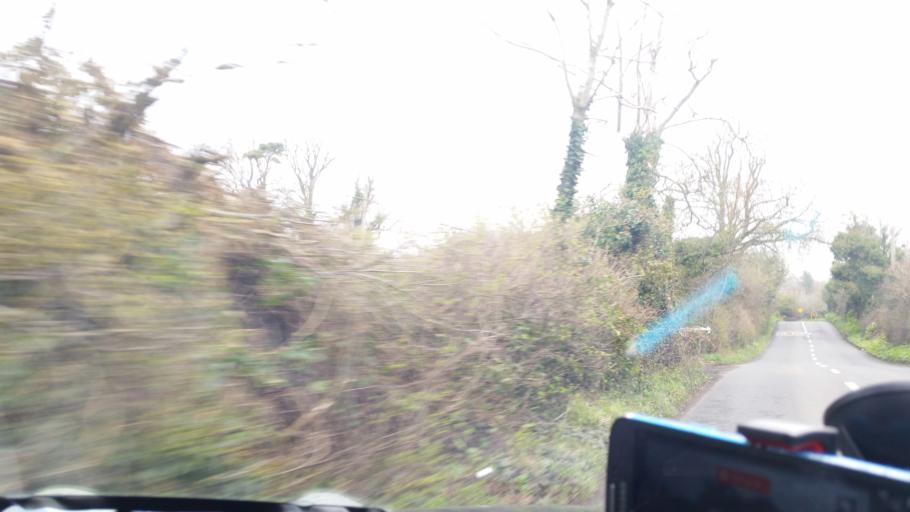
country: IE
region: Leinster
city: Portmarnock
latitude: 53.4268
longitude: -6.1548
